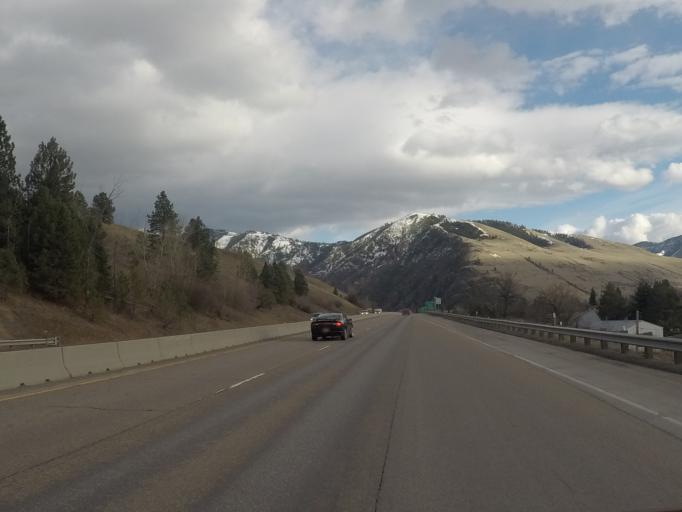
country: US
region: Montana
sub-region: Missoula County
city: Missoula
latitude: 46.8773
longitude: -113.9896
